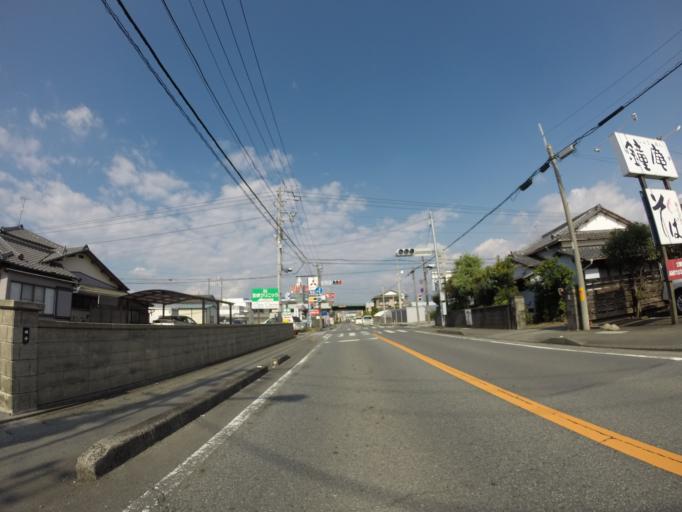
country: JP
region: Shizuoka
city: Fuji
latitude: 35.1703
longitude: 138.6485
